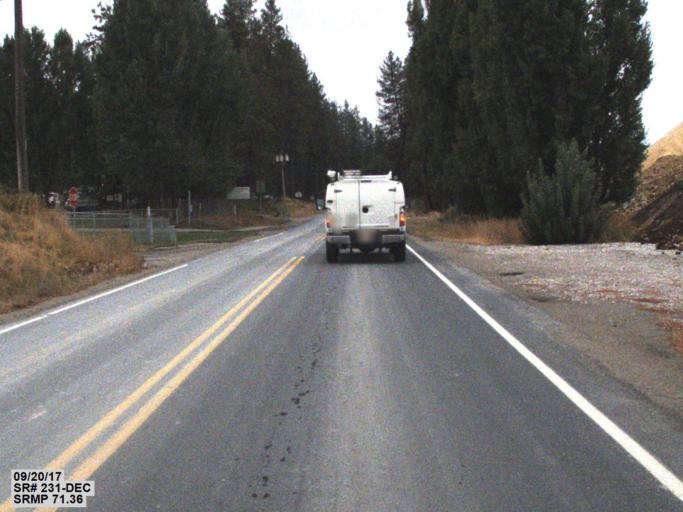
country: US
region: Washington
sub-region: Stevens County
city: Chewelah
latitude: 48.1694
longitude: -117.7228
